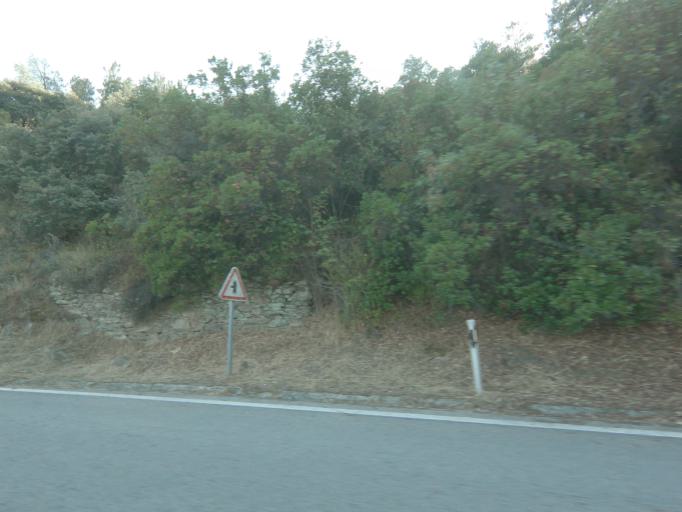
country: PT
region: Viseu
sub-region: Tabuaco
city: Tabuaco
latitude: 41.1227
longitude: -7.5720
